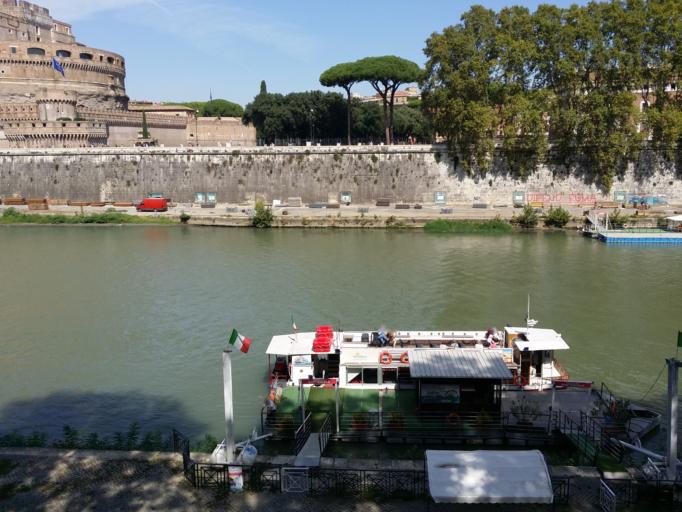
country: VA
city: Vatican City
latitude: 41.9014
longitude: 12.4681
